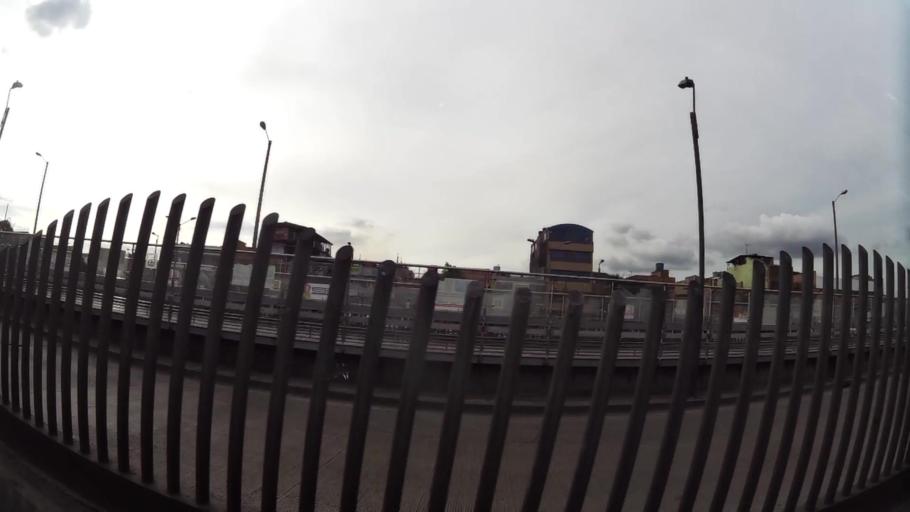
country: CO
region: Cundinamarca
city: Soacha
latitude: 4.6379
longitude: -74.1592
